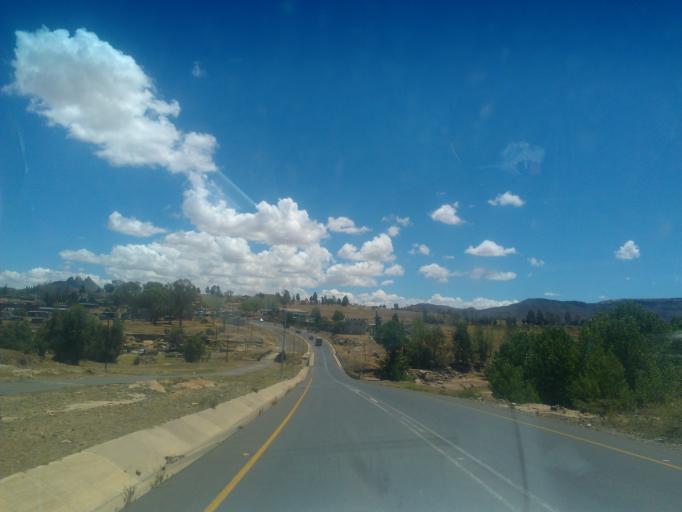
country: LS
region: Mafeteng
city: Mafeteng
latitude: -29.6882
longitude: 27.4388
